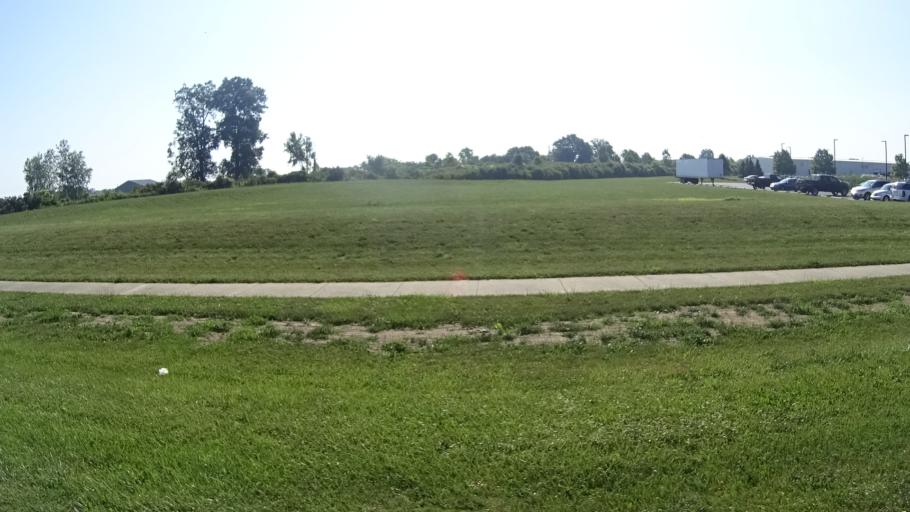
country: US
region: Ohio
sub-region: Erie County
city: Huron
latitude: 41.3992
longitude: -82.5911
